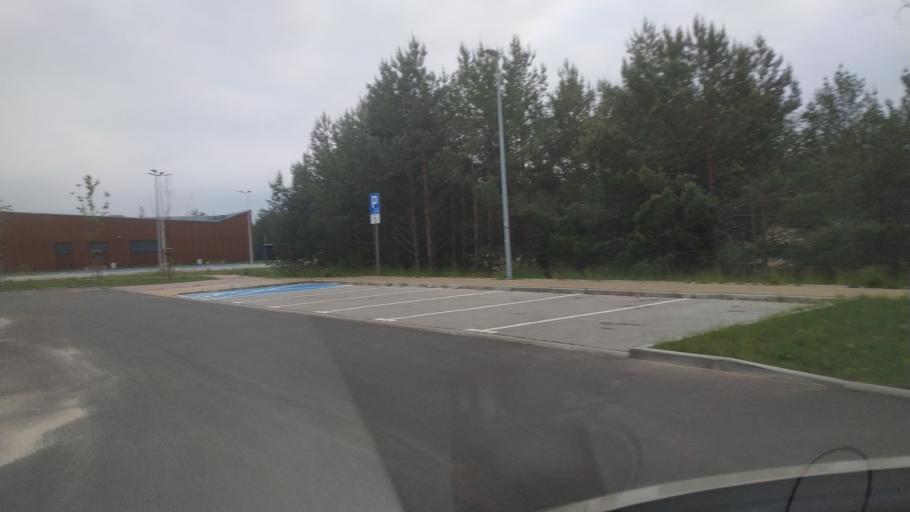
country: PL
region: Kujawsko-Pomorskie
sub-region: Torun
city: Torun
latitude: 53.0507
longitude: 18.6001
